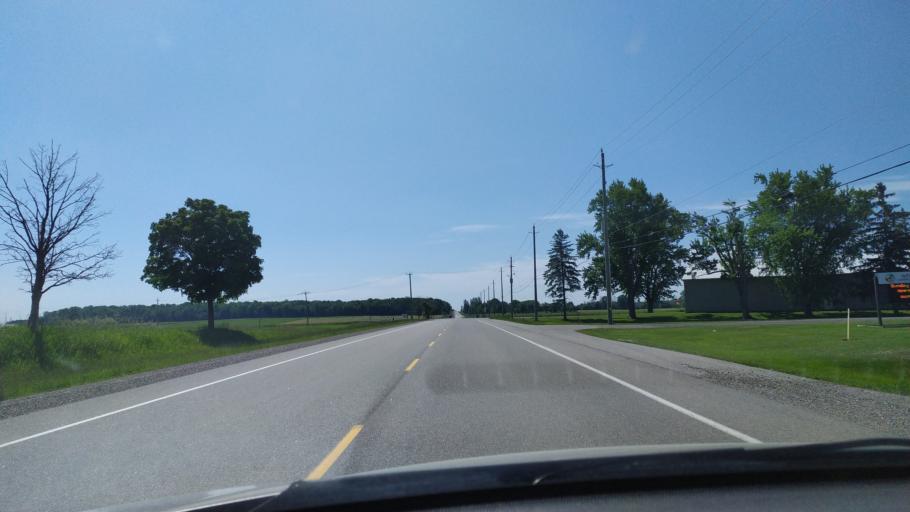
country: CA
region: Ontario
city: Stratford
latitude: 43.4549
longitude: -80.7568
